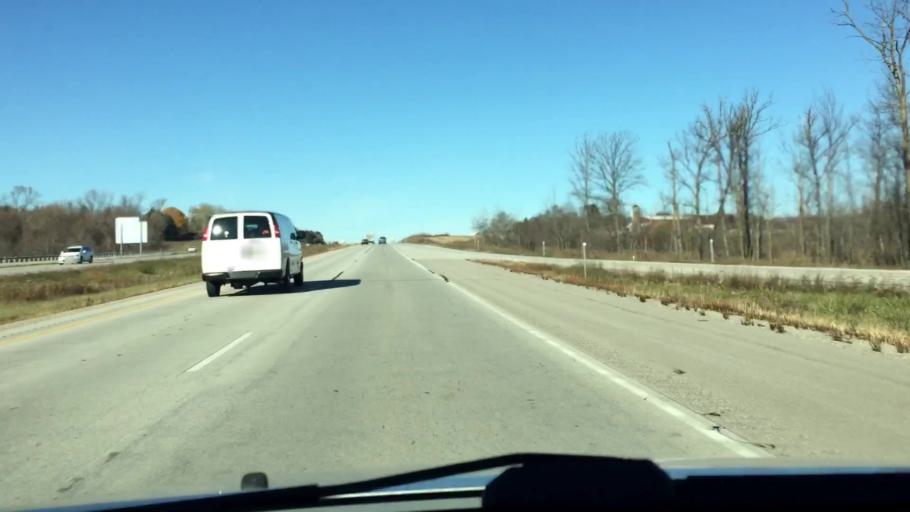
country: US
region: Wisconsin
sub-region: Brown County
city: Howard
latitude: 44.5621
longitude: -88.1339
